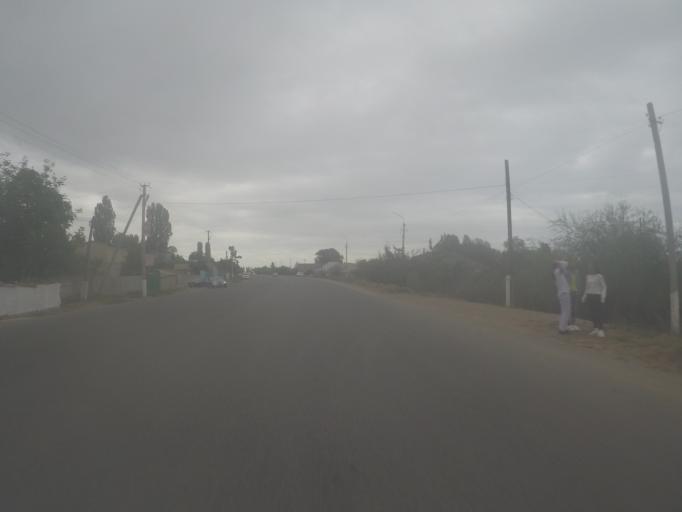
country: KG
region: Ysyk-Koel
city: Cholpon-Ata
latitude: 42.6907
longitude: 77.3622
